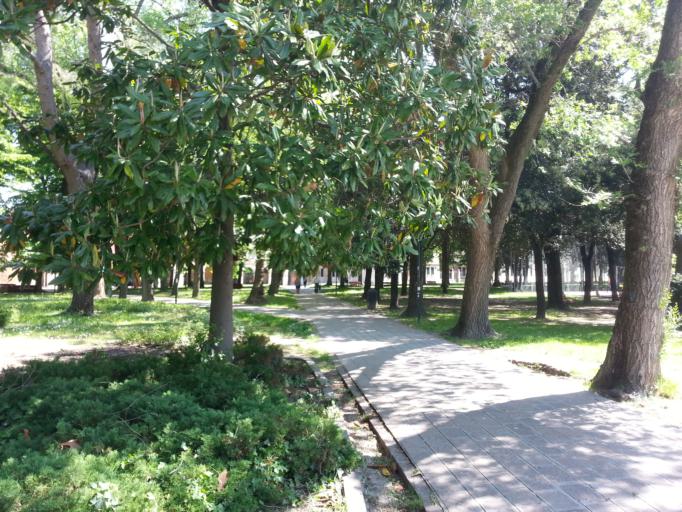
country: IT
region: Veneto
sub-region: Provincia di Venezia
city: Lido
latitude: 45.4258
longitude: 12.3610
